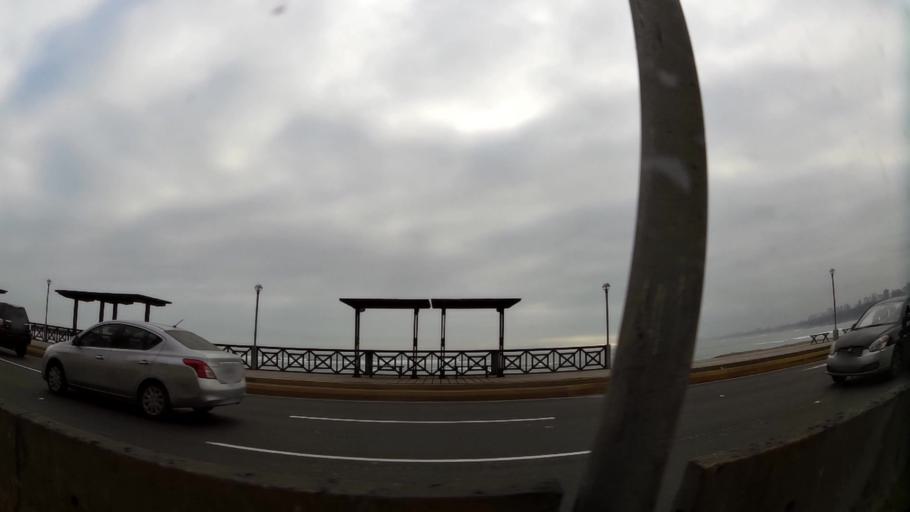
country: PE
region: Lima
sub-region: Lima
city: Surco
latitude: -12.1509
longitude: -77.0246
